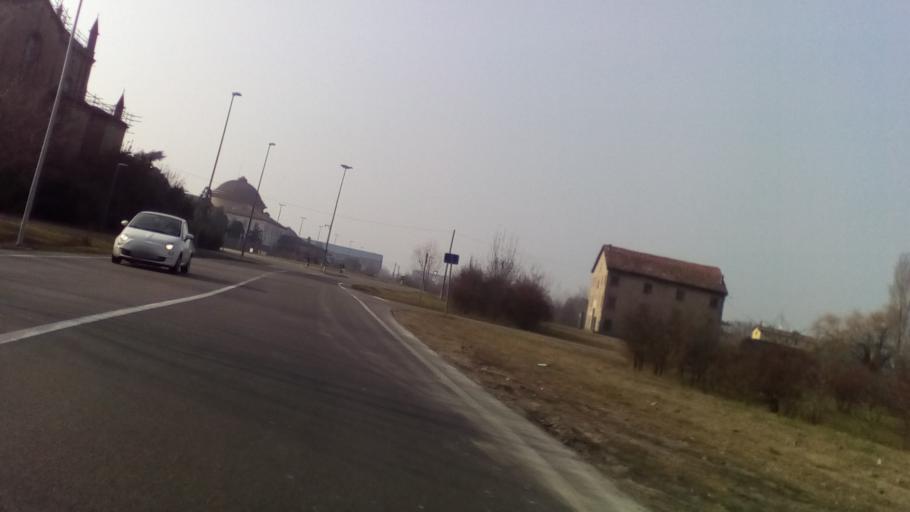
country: IT
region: Emilia-Romagna
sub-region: Provincia di Modena
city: Modena
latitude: 44.6593
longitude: 10.9130
